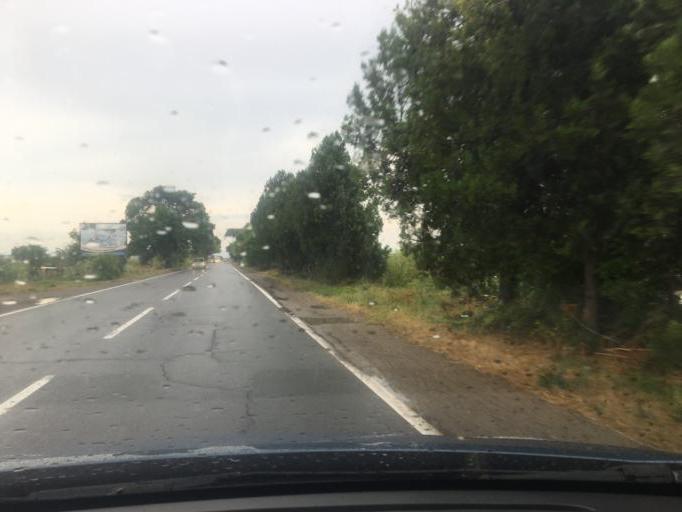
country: BG
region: Burgas
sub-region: Obshtina Pomorie
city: Pomorie
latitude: 42.5704
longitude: 27.6053
